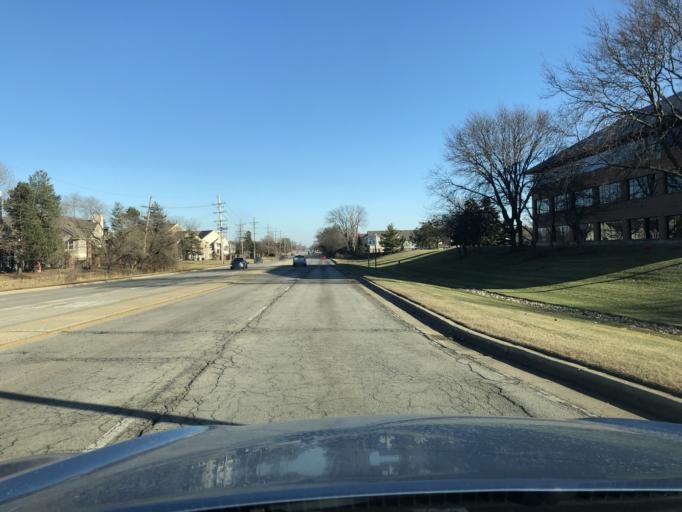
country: US
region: Illinois
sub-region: DuPage County
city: Itasca
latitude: 41.9924
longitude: -88.0200
